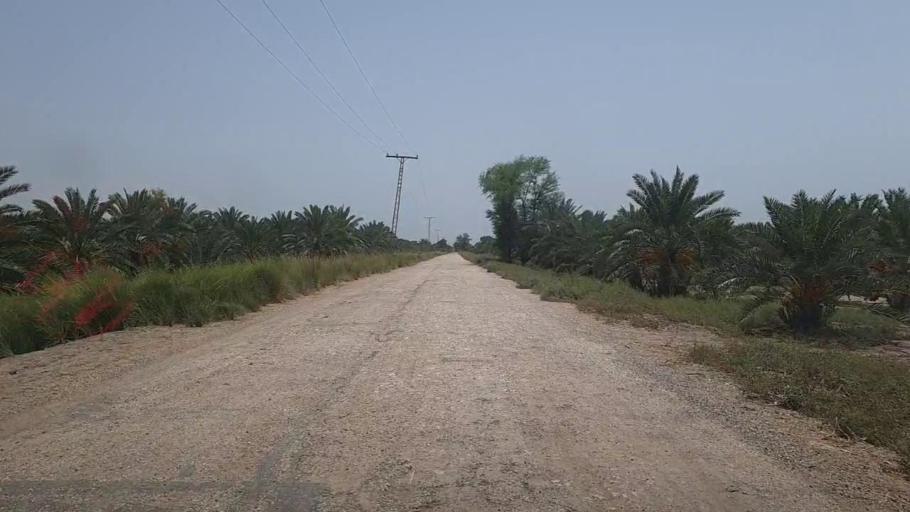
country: PK
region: Sindh
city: Pad Idan
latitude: 26.8495
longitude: 68.3248
